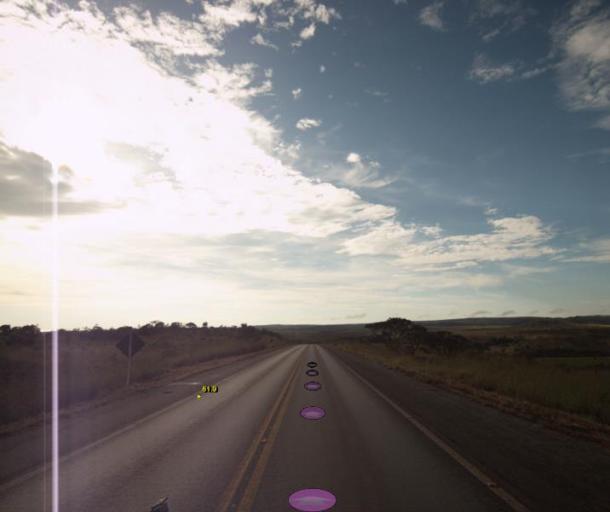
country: BR
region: Goias
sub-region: Pirenopolis
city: Pirenopolis
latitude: -15.7661
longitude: -48.7241
